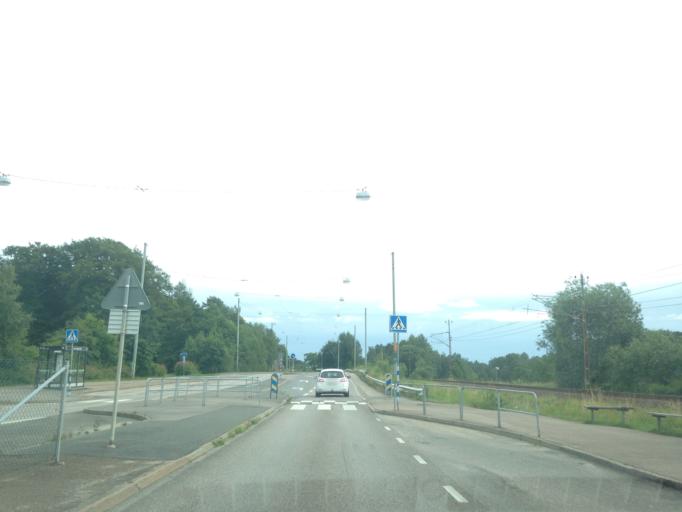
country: SE
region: Vaestra Goetaland
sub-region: Goteborg
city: Goeteborg
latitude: 57.7496
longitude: 11.9497
